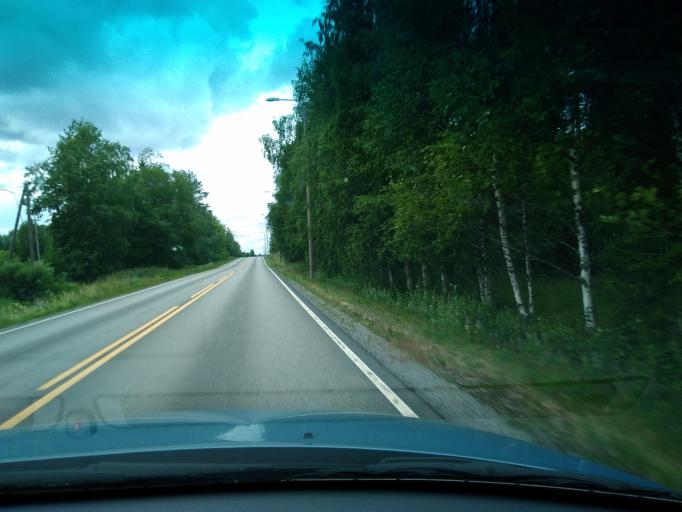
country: FI
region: Central Finland
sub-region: Saarijaervi-Viitasaari
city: Pylkoenmaeki
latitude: 62.6462
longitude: 24.9312
